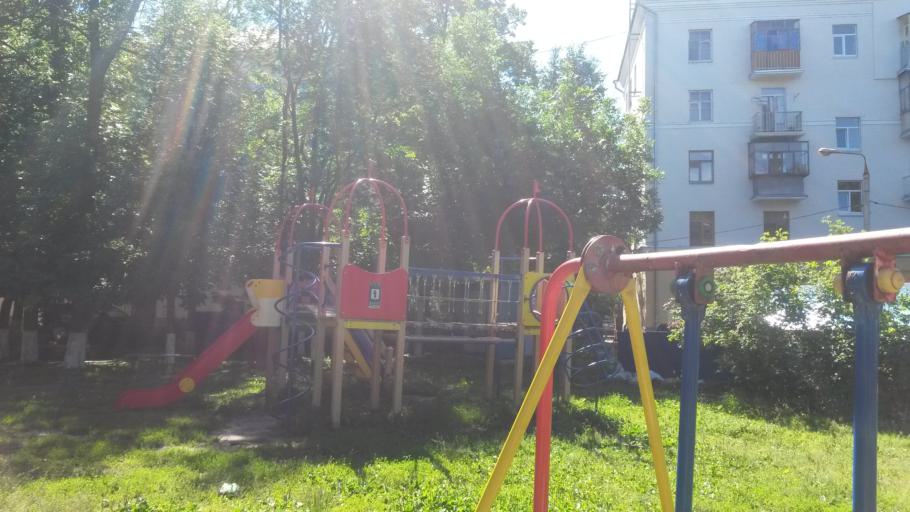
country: RU
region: Jaroslavl
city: Yaroslavl
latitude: 57.6359
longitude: 39.8628
